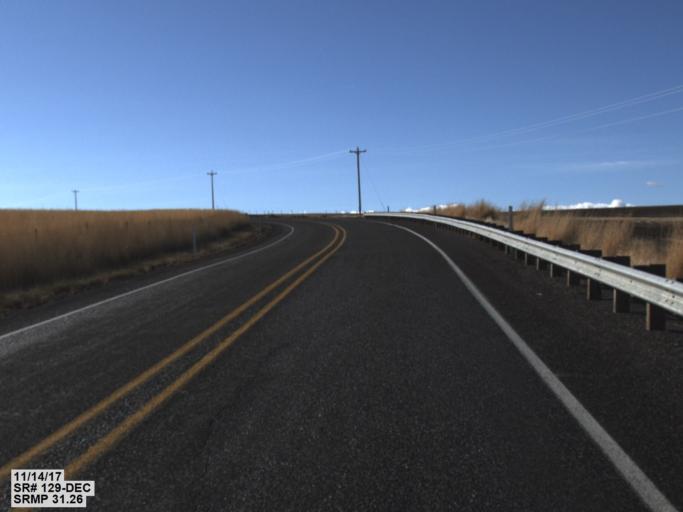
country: US
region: Washington
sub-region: Asotin County
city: Asotin
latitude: 46.3091
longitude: -117.0424
